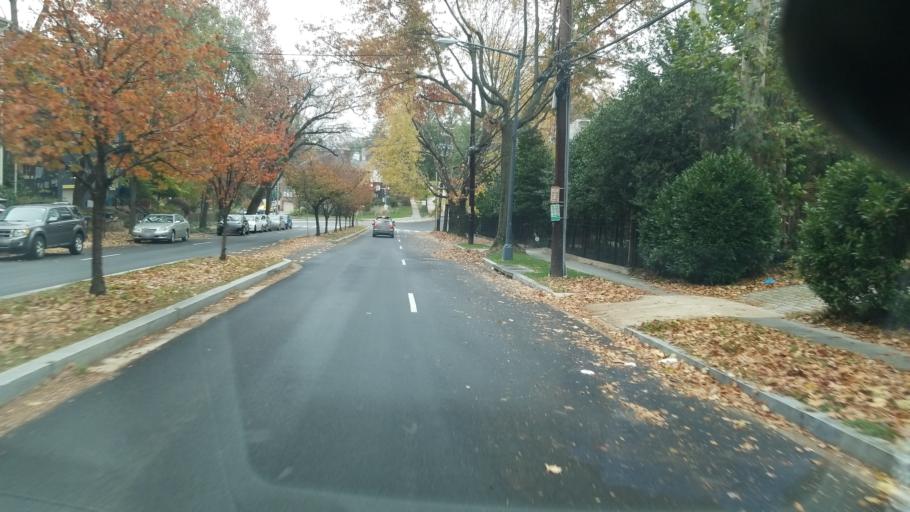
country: US
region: Washington, D.C.
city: Washington, D.C.
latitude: 38.9239
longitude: -77.0587
